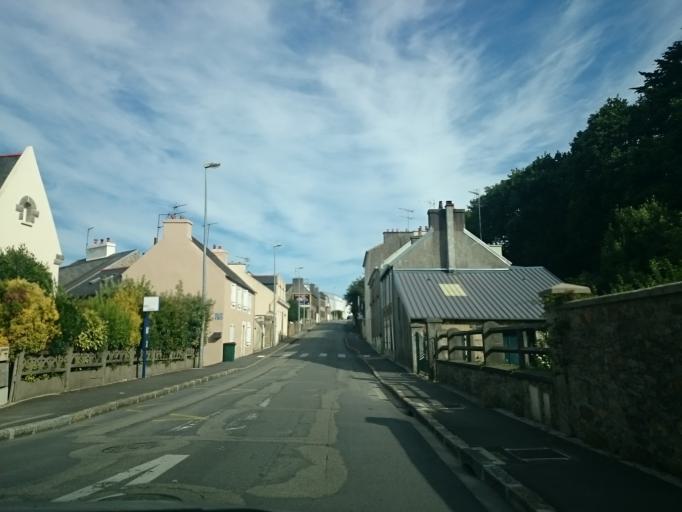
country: FR
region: Brittany
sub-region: Departement du Finistere
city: Brest
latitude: 48.4174
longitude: -4.4943
